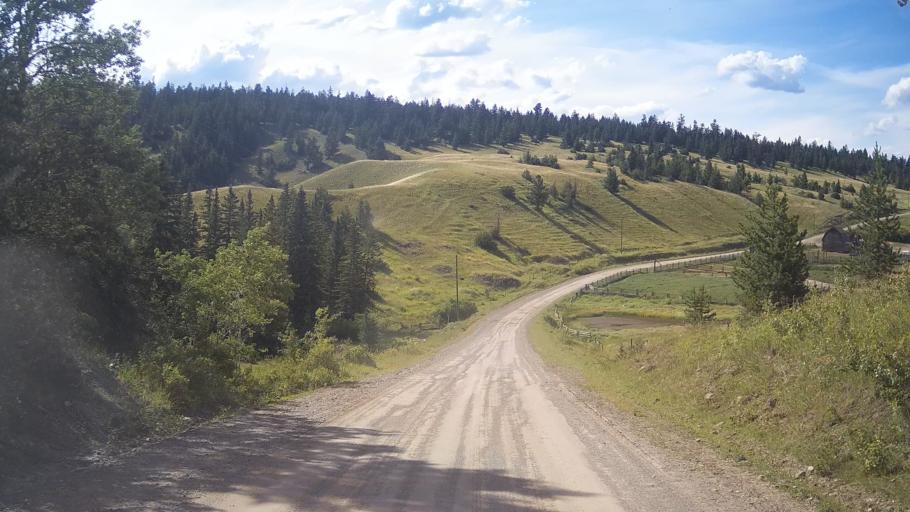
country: CA
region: British Columbia
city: Lillooet
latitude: 51.3026
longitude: -121.9848
